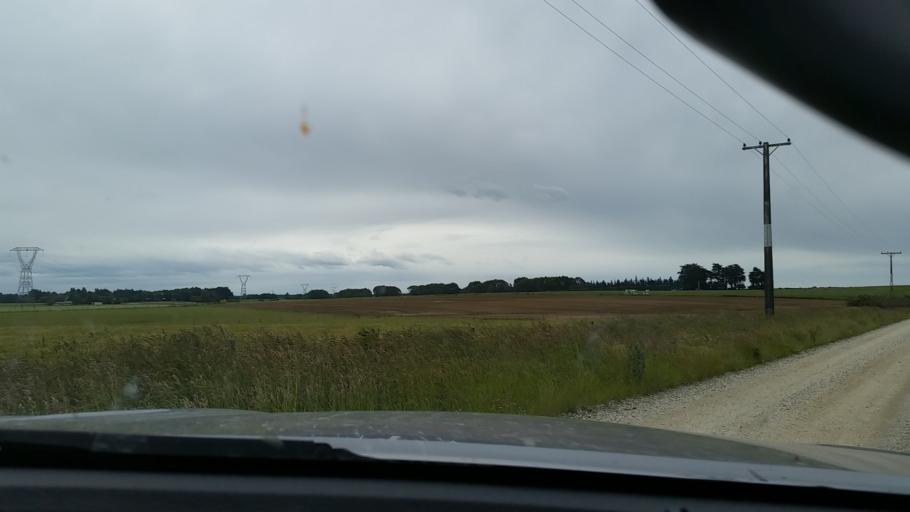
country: NZ
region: Southland
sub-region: Invercargill City
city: Invercargill
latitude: -46.2749
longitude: 168.5007
